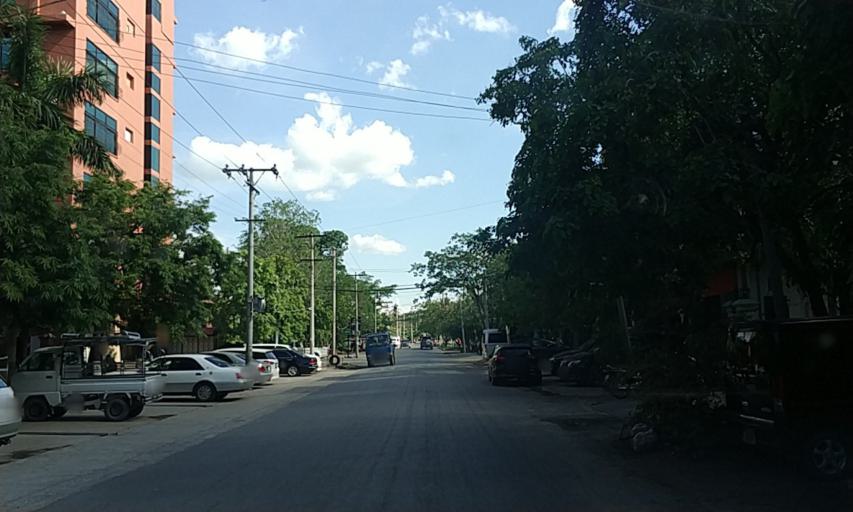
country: MM
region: Mandalay
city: Mandalay
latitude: 21.9737
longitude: 96.1078
